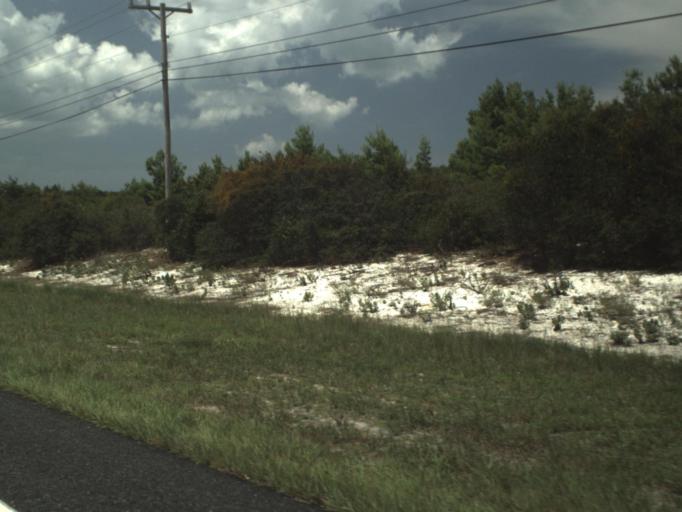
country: US
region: Florida
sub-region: Palm Beach County
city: Tequesta
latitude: 27.0127
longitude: -80.1038
